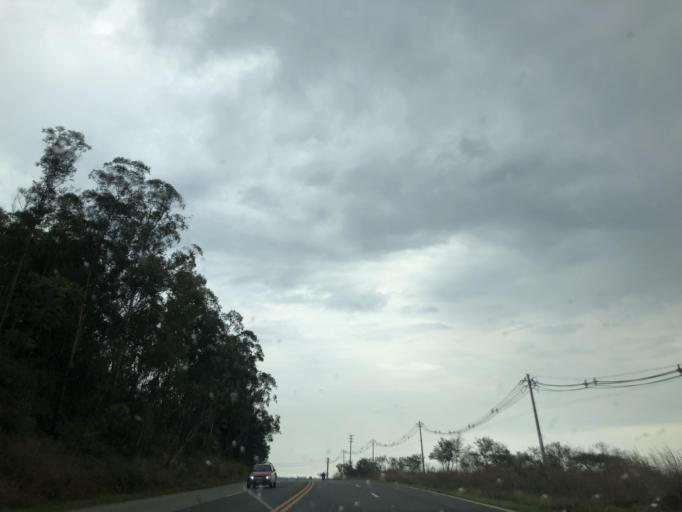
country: BR
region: Sao Paulo
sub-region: Salto De Pirapora
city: Salto de Pirapora
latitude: -23.6594
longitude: -47.5904
